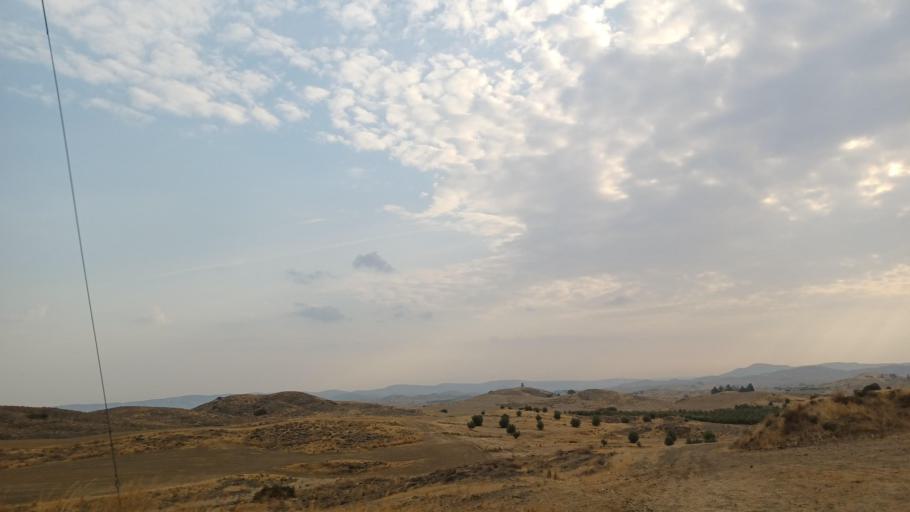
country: CY
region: Larnaka
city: Troulloi
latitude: 35.0170
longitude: 33.5750
